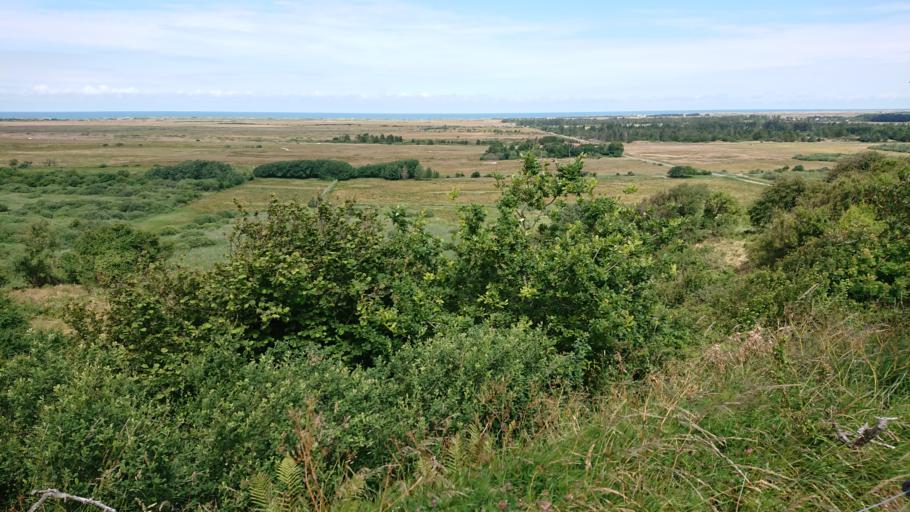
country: DK
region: North Denmark
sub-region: Jammerbugt Kommune
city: Brovst
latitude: 57.1325
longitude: 9.4085
